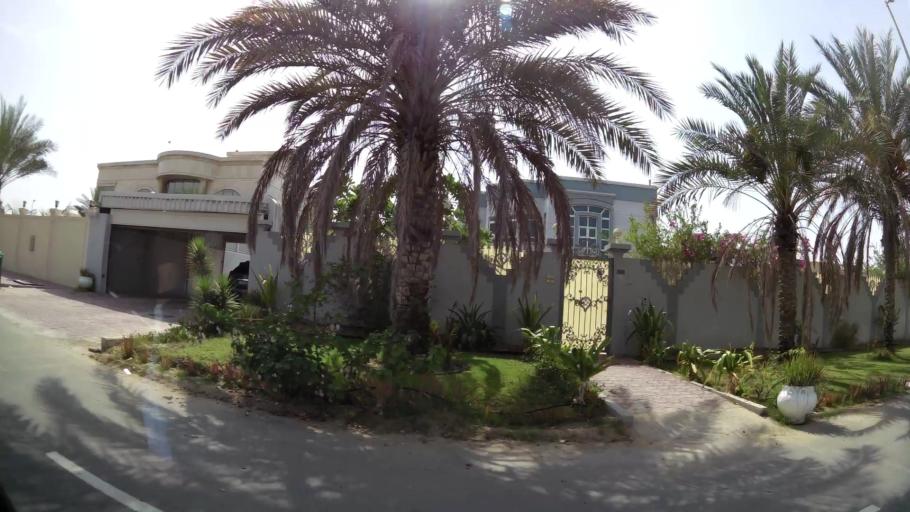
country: AE
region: Ash Shariqah
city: Sharjah
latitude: 25.2493
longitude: 55.4423
